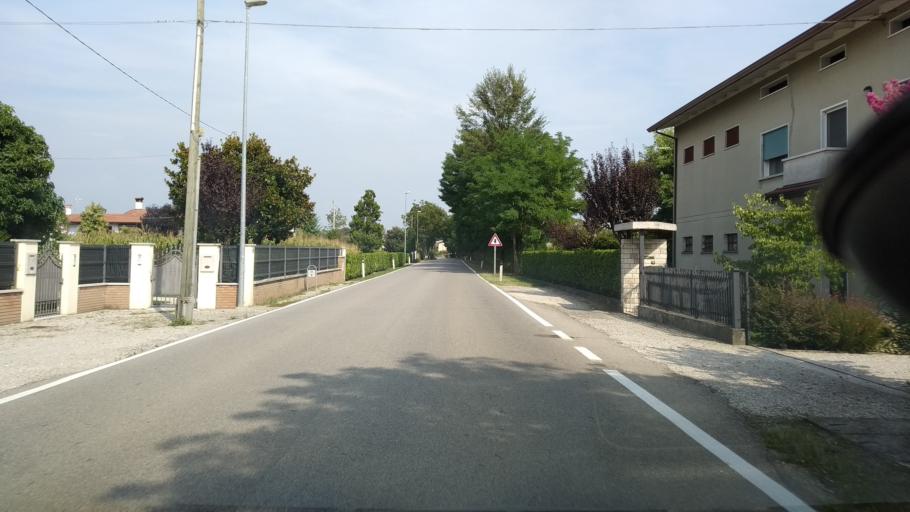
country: IT
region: Veneto
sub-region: Provincia di Padova
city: Fontaniva
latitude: 45.6613
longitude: 11.7483
